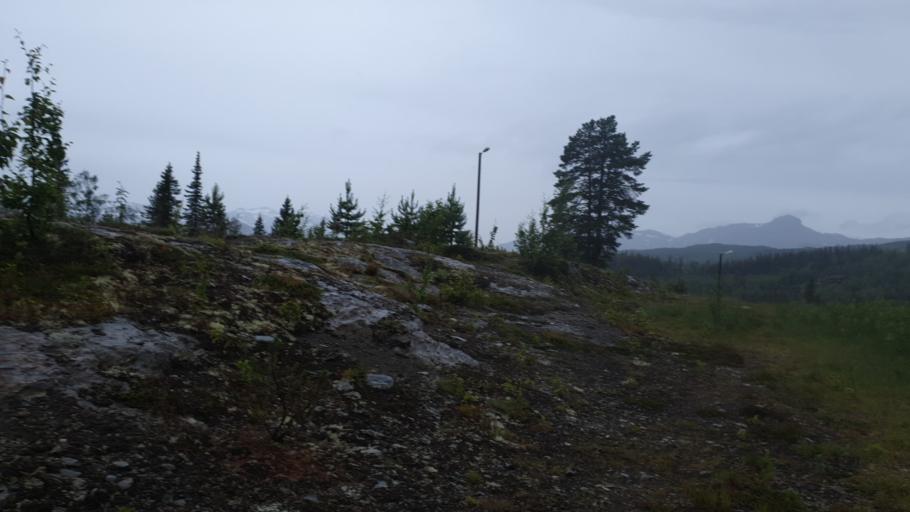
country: NO
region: Oppland
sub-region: Vestre Slidre
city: Slidre
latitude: 61.2305
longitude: 8.9126
